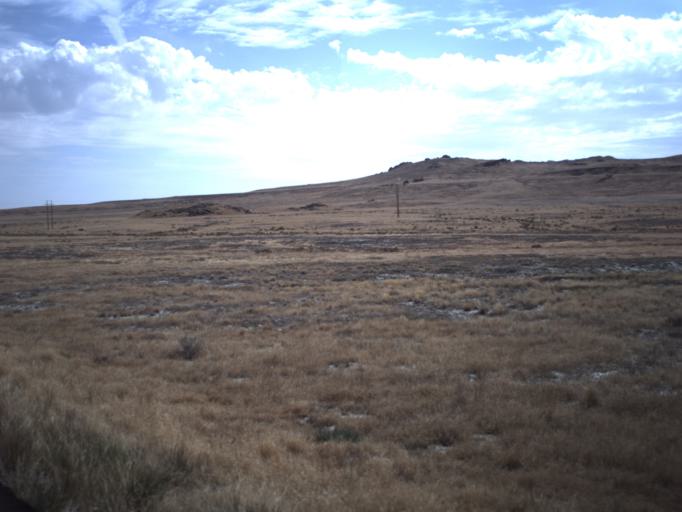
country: US
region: Utah
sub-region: Tooele County
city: Wendover
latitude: 41.4099
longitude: -113.9303
